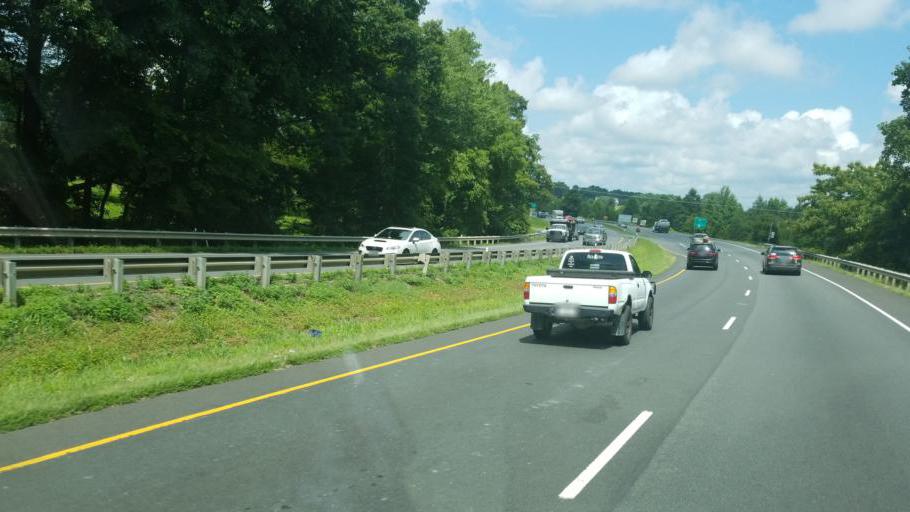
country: US
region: Virginia
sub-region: Fauquier County
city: Warrenton
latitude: 38.6763
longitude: -77.7880
